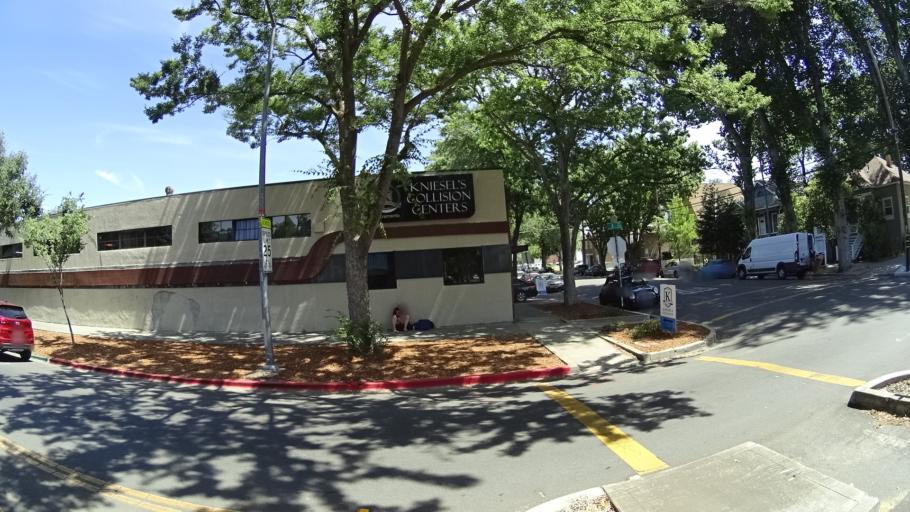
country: US
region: California
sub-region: Sacramento County
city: Sacramento
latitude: 38.5829
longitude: -121.4804
